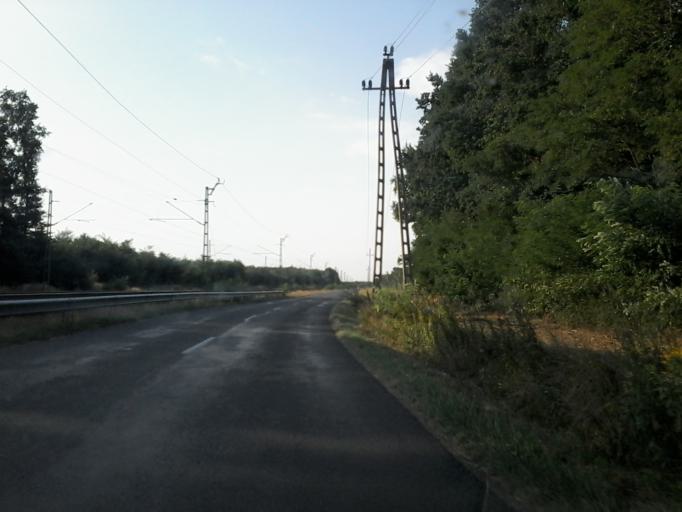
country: HU
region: Vas
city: Janoshaza
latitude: 47.0978
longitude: 17.1825
